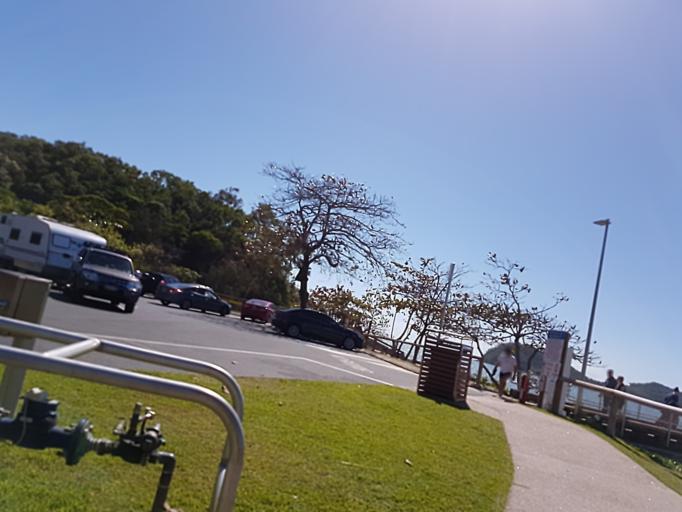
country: AU
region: Queensland
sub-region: Cairns
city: Palm Cove
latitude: -16.7400
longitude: 145.6717
